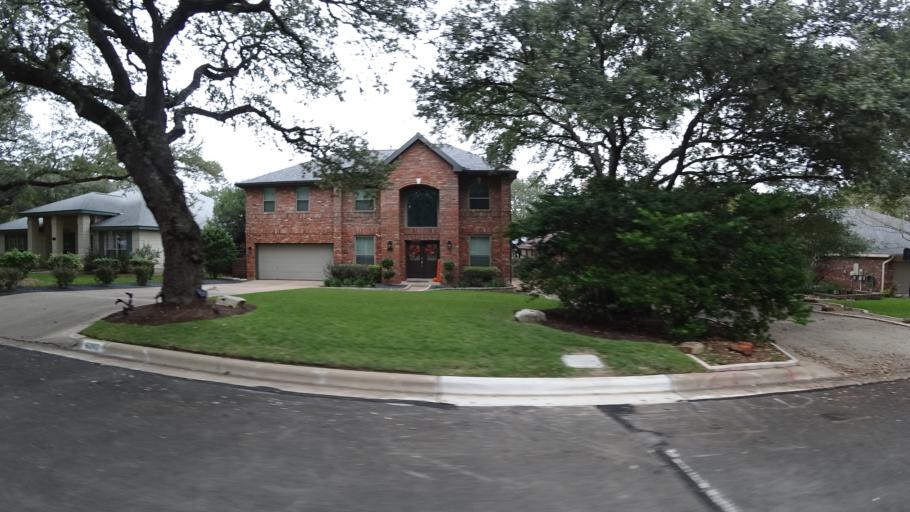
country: US
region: Texas
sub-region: Travis County
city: Shady Hollow
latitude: 30.1871
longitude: -97.8923
